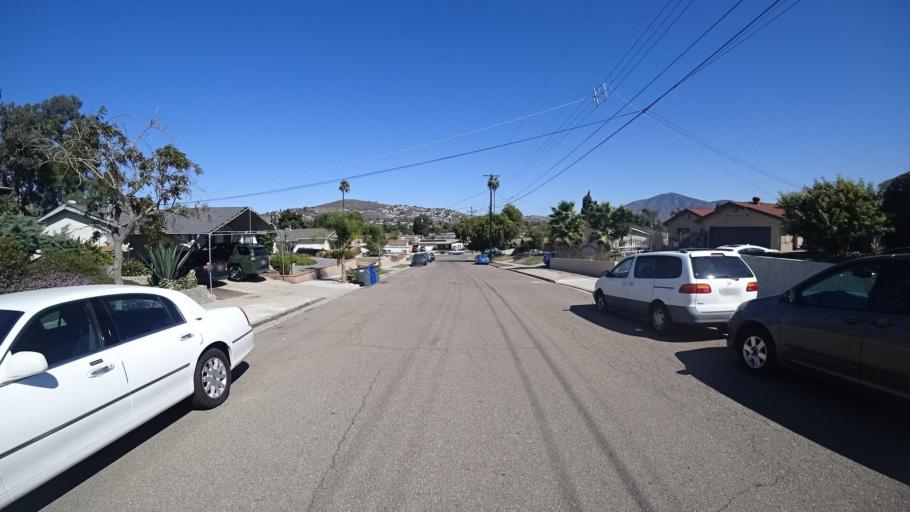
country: US
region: California
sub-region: San Diego County
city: La Presa
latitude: 32.7101
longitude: -117.0175
